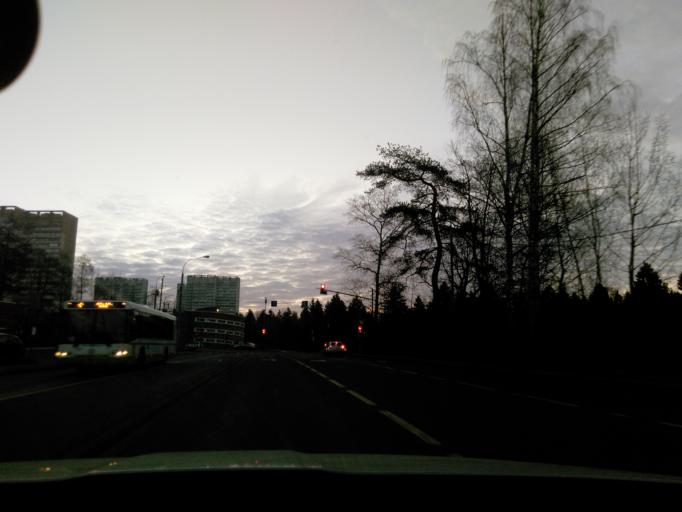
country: RU
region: Moscow
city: Zelenograd
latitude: 55.9917
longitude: 37.1847
